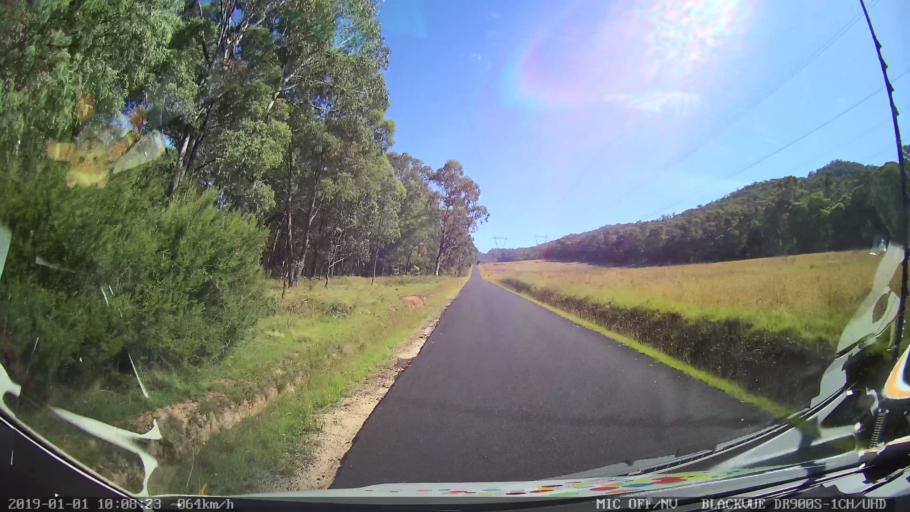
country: AU
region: New South Wales
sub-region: Snowy River
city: Jindabyne
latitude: -36.1600
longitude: 148.1575
